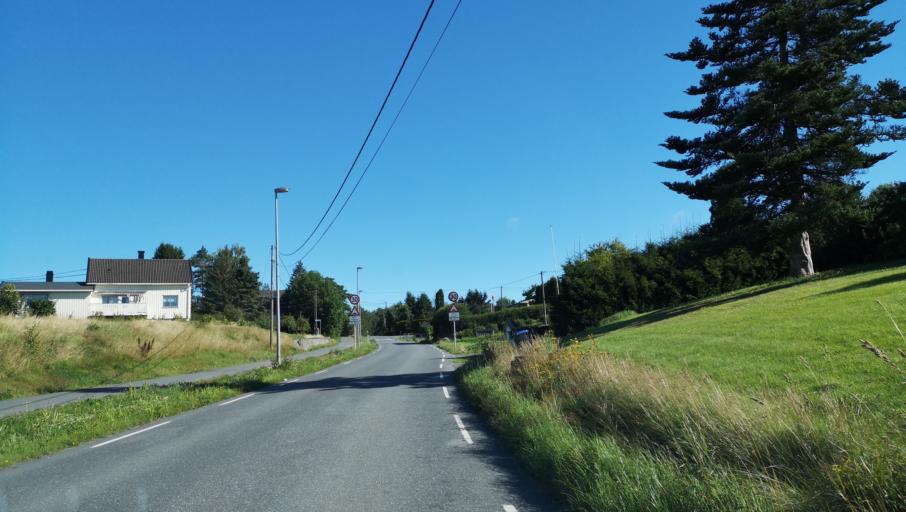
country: NO
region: Ostfold
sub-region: Hobol
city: Knappstad
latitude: 59.6231
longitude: 11.0241
